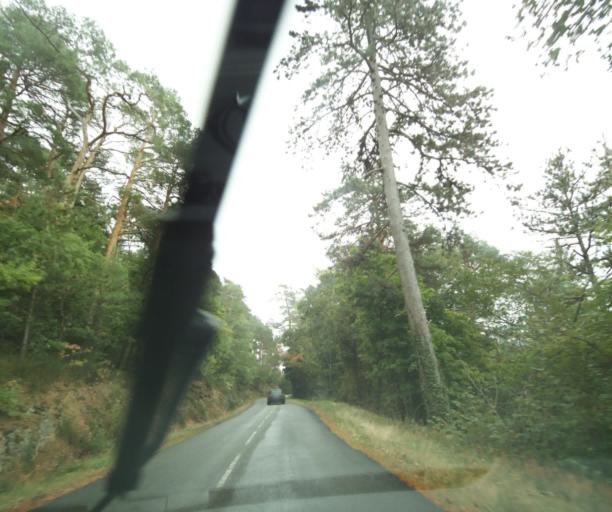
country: FR
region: Auvergne
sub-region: Departement du Puy-de-Dome
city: Durtol
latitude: 45.7946
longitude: 3.0332
